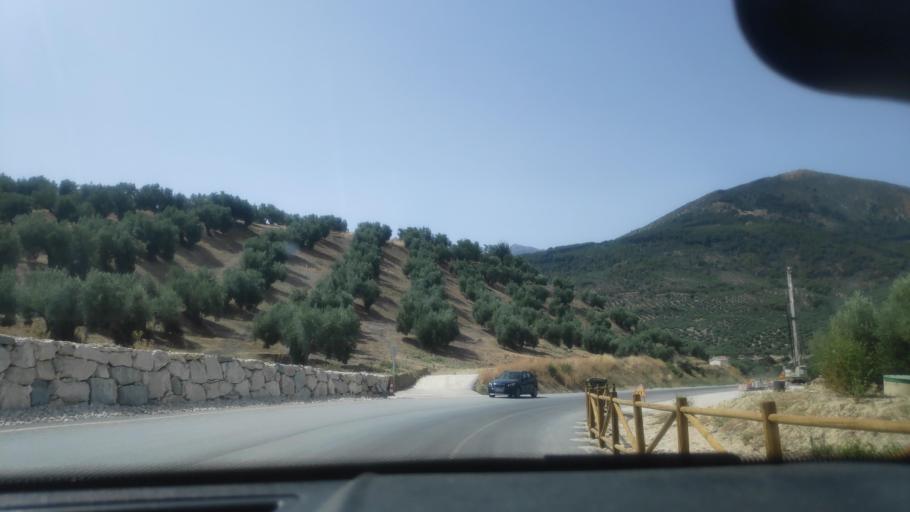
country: ES
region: Andalusia
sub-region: Provincia de Jaen
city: Jodar
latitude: 37.8045
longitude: -3.4122
